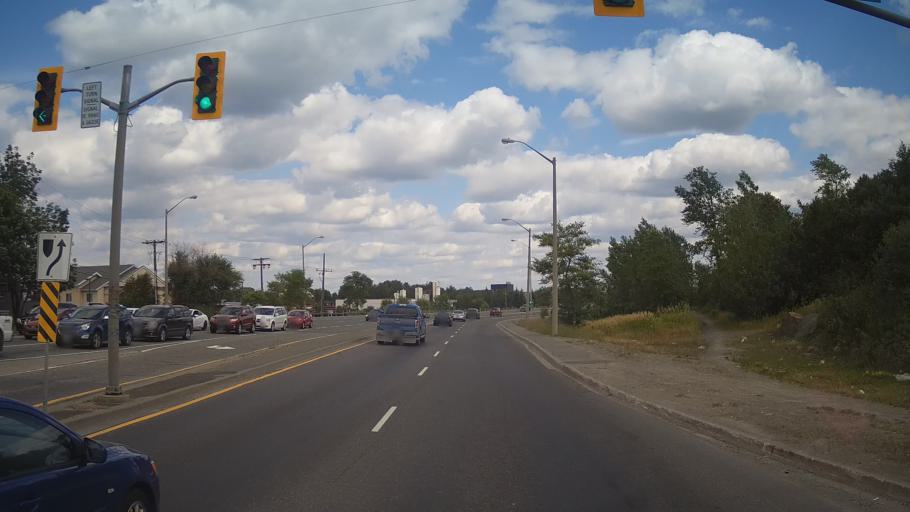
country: CA
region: Ontario
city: Greater Sudbury
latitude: 46.5055
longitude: -80.9439
